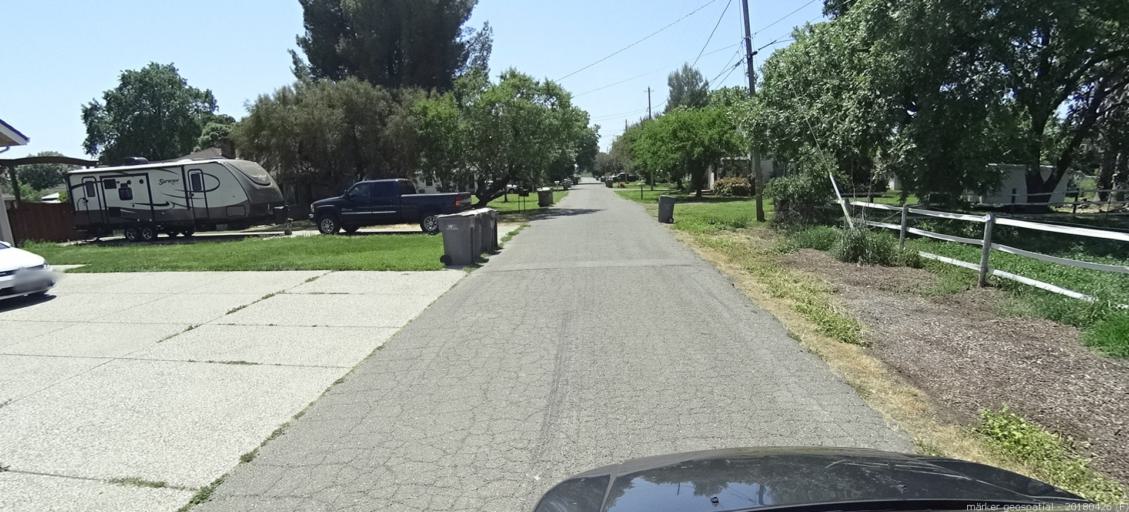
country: US
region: California
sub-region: Yolo County
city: West Sacramento
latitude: 38.5345
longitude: -121.5454
